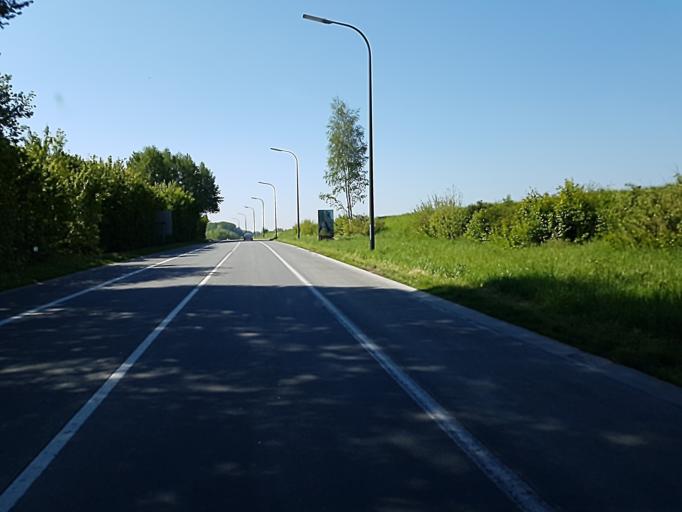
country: BE
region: Wallonia
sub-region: Province du Hainaut
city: Ath
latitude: 50.6756
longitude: 3.7992
